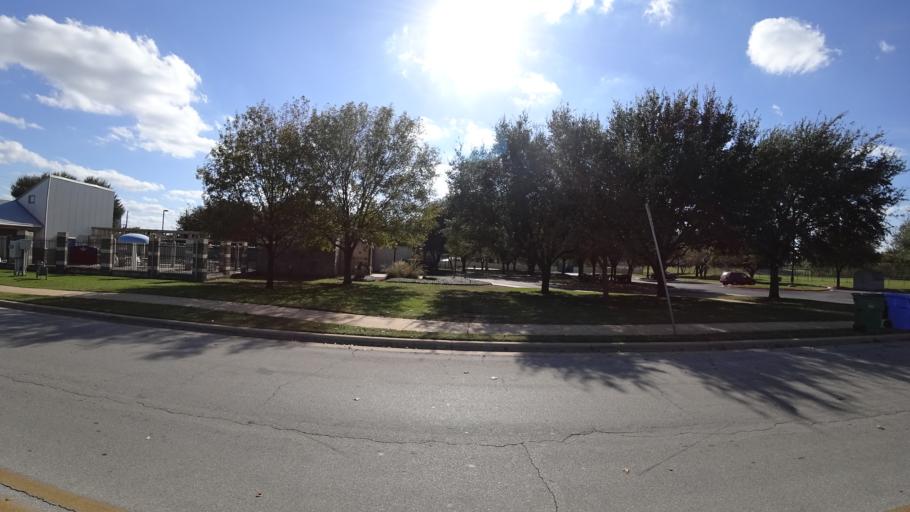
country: US
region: Texas
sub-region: Travis County
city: Wells Branch
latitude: 30.4557
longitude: -97.6799
